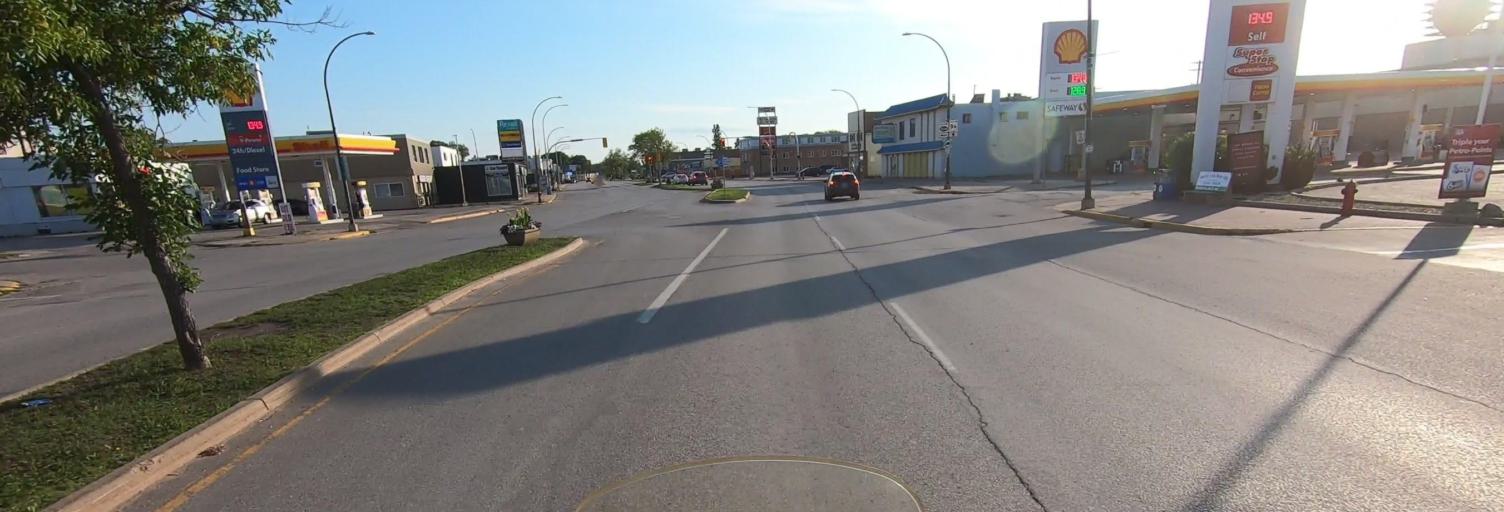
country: CA
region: Manitoba
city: Selkirk
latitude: 50.1449
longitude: -96.8731
